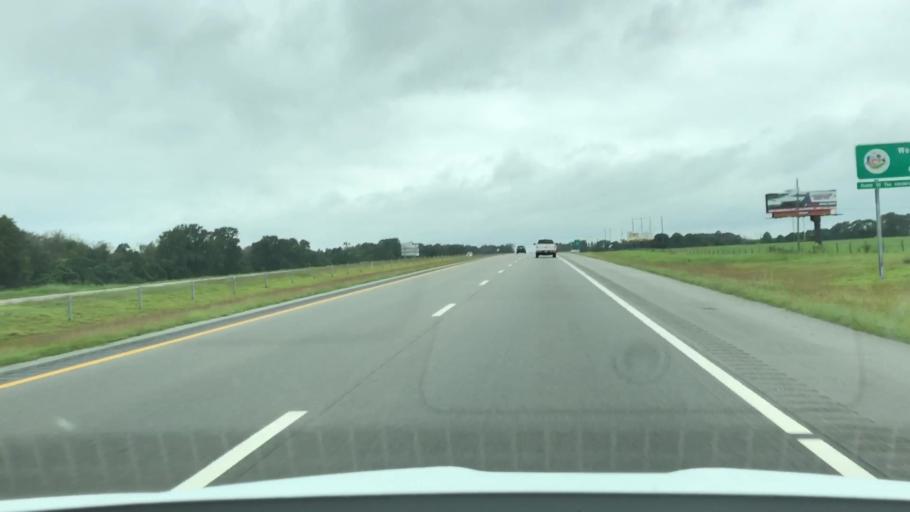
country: US
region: North Carolina
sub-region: Lenoir County
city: La Grange
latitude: 35.3124
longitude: -77.8259
